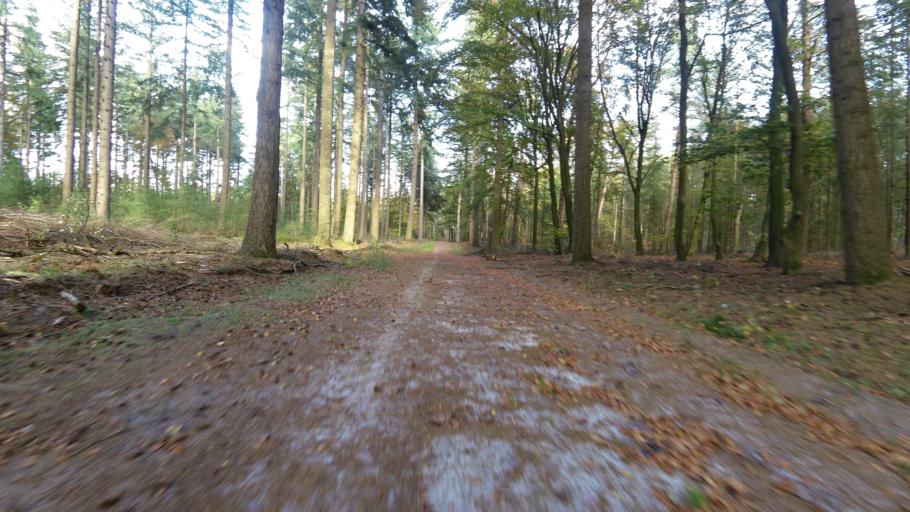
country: NL
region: Gelderland
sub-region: Gemeente Heerde
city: Heerde
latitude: 52.4171
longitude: 6.0353
